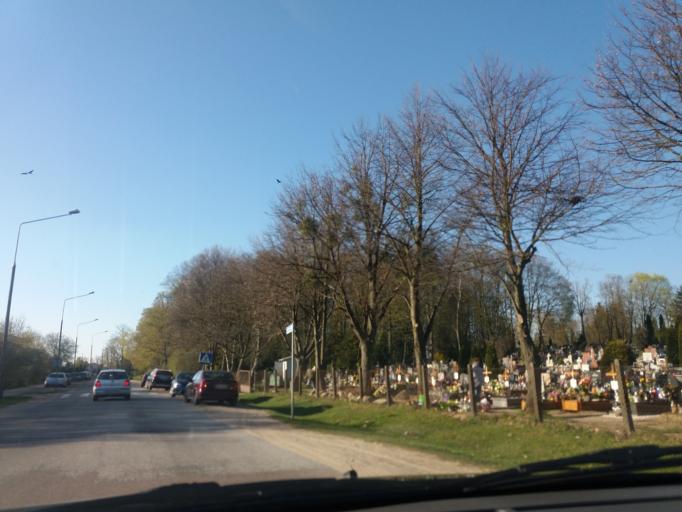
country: PL
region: Warmian-Masurian Voivodeship
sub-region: Powiat nidzicki
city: Nidzica
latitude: 53.3486
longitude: 20.4309
